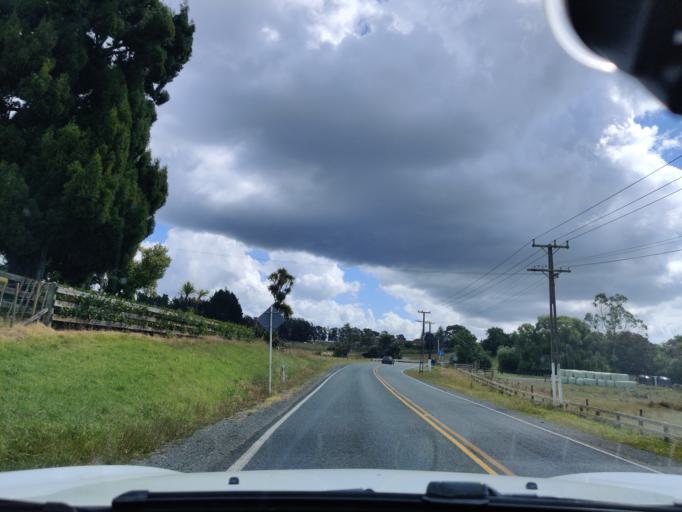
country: NZ
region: Auckland
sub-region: Auckland
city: Red Hill
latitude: -37.0389
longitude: 174.9924
